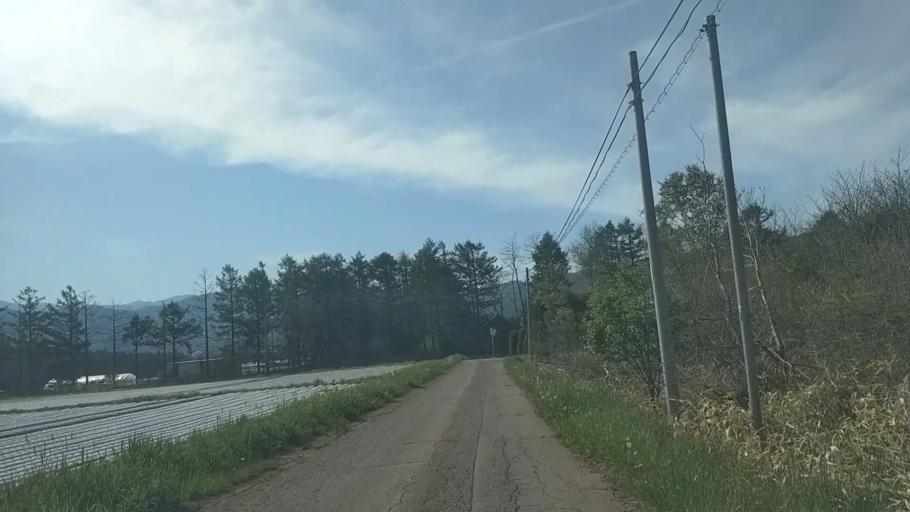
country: JP
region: Yamanashi
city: Nirasaki
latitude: 35.9485
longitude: 138.4603
